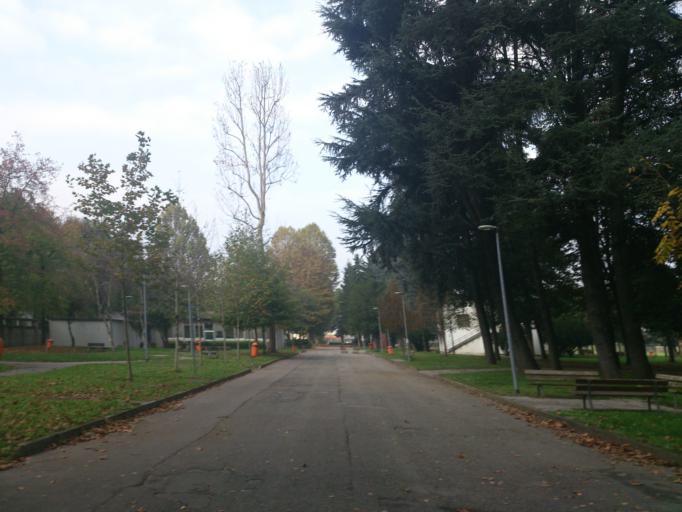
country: IT
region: Lombardy
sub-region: Citta metropolitana di Milano
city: San Donato Milanese
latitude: 45.4265
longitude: 9.2605
